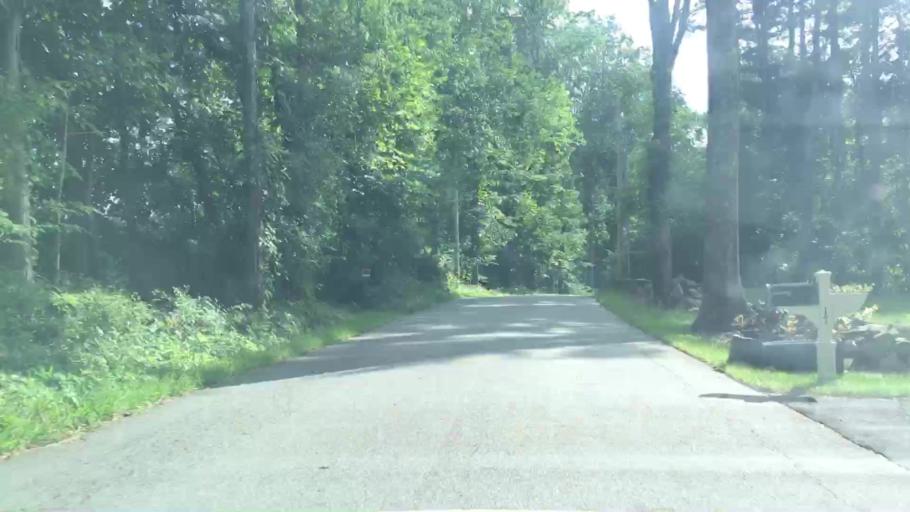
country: US
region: New Hampshire
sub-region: Strafford County
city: Madbury
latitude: 43.1639
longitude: -70.9169
